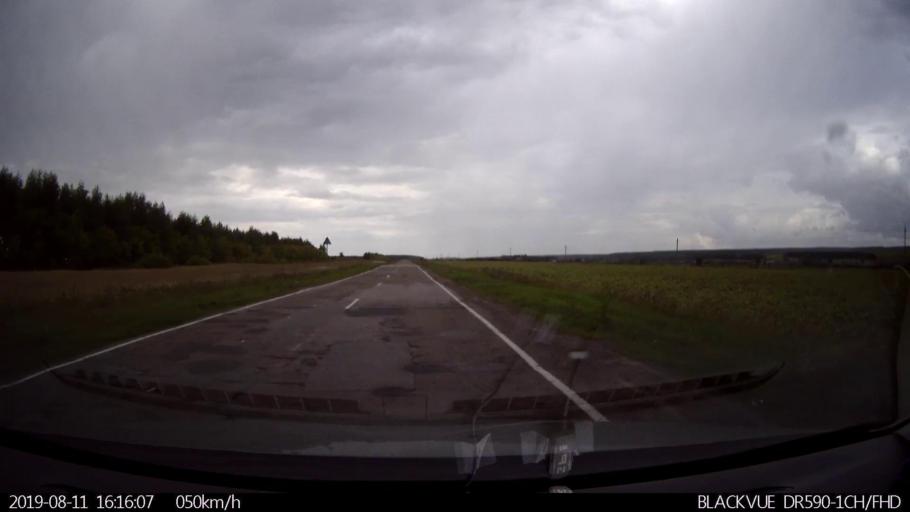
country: RU
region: Ulyanovsk
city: Mayna
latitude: 54.0389
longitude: 47.6229
